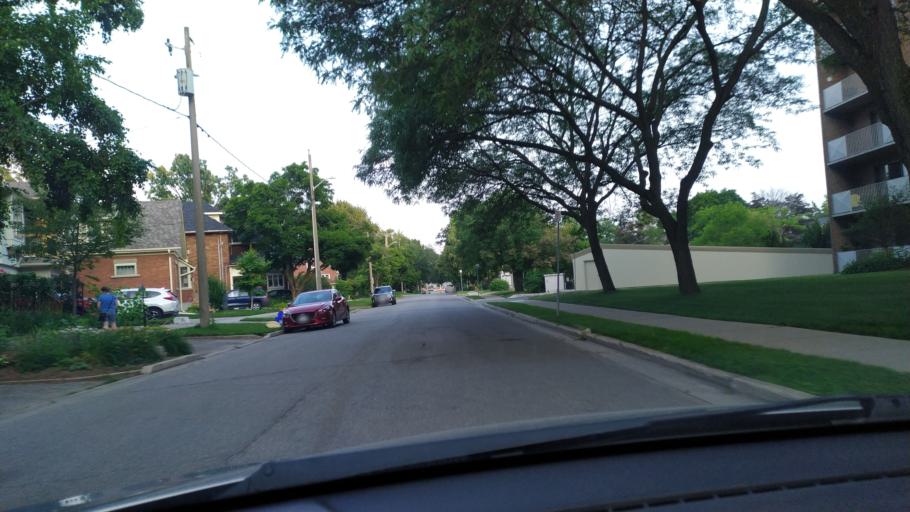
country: CA
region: Ontario
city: Waterloo
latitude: 43.4557
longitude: -80.5160
